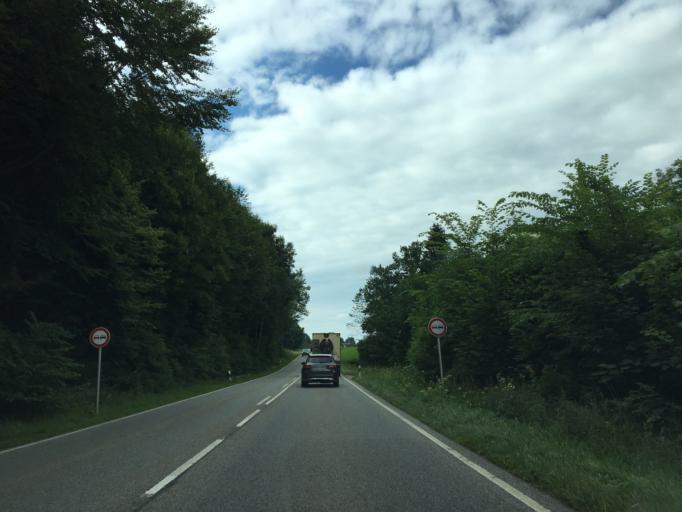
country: DE
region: Bavaria
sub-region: Upper Bavaria
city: Warngau
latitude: 47.8041
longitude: 11.7199
